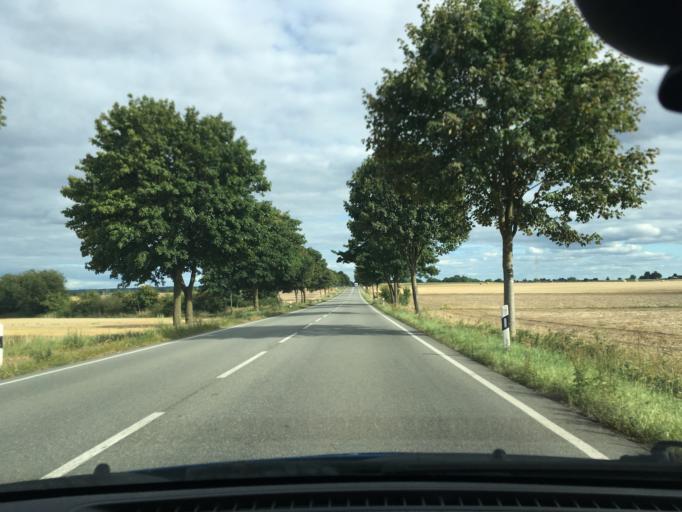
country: DE
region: Lower Saxony
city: Neu Wulmstorf
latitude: 53.4386
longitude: 9.7672
